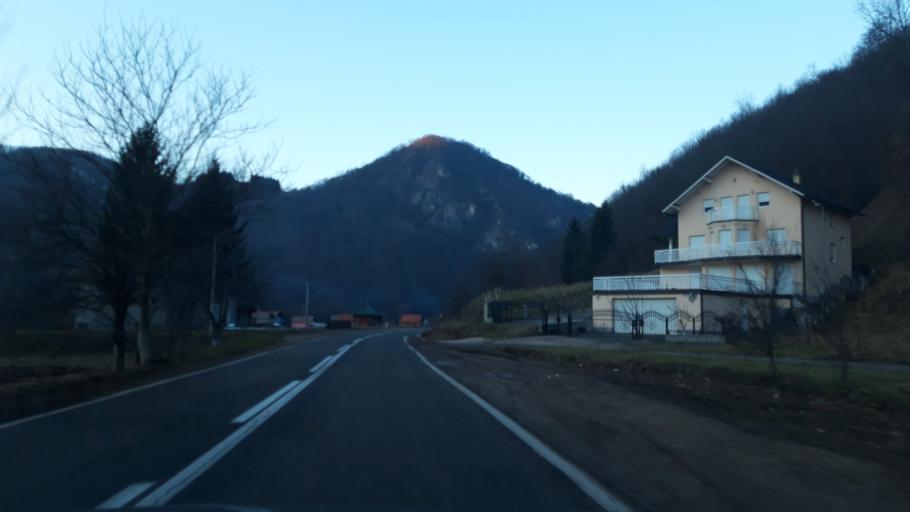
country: BA
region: Republika Srpska
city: Milici
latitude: 44.2615
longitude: 19.1047
